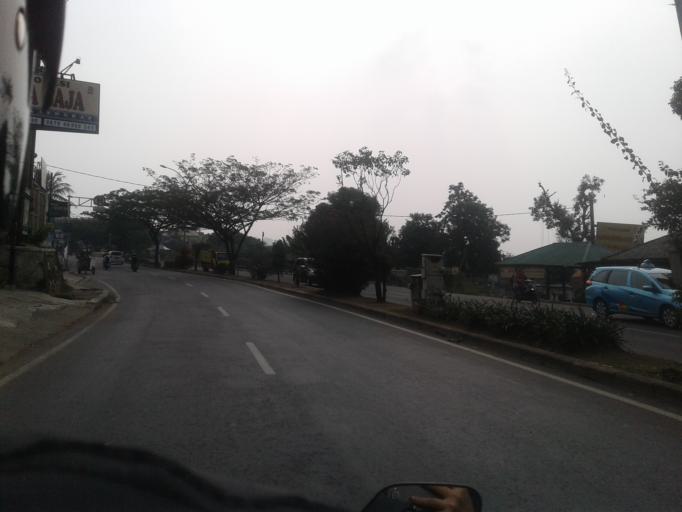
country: ID
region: West Java
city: Depok
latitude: -6.3802
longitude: 106.8539
